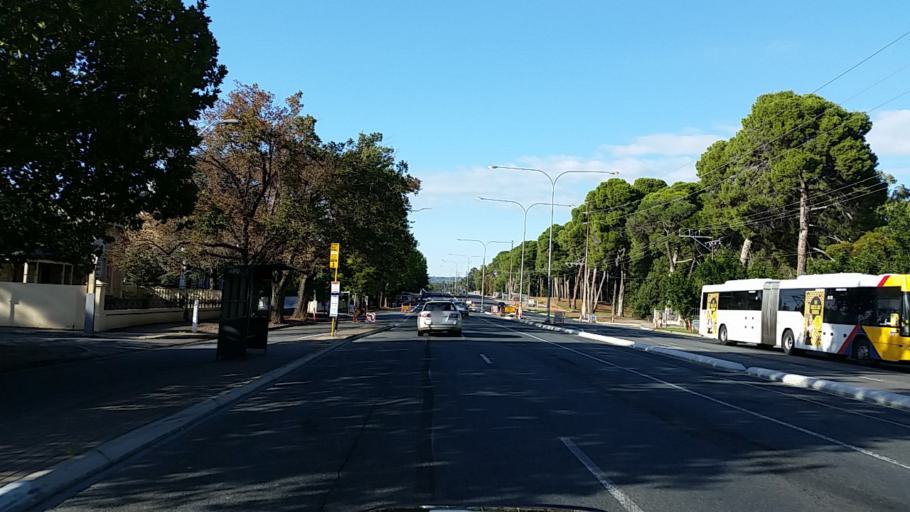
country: AU
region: South Australia
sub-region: Adelaide
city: North Adelaide
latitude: -34.9112
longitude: 138.6132
